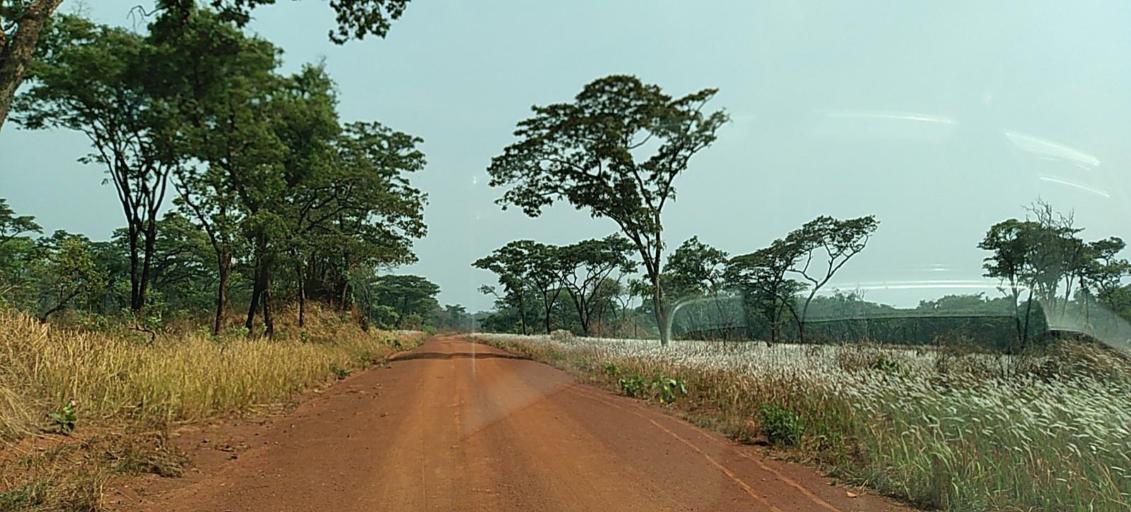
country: ZM
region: North-Western
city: Kansanshi
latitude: -12.0236
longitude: 26.8510
